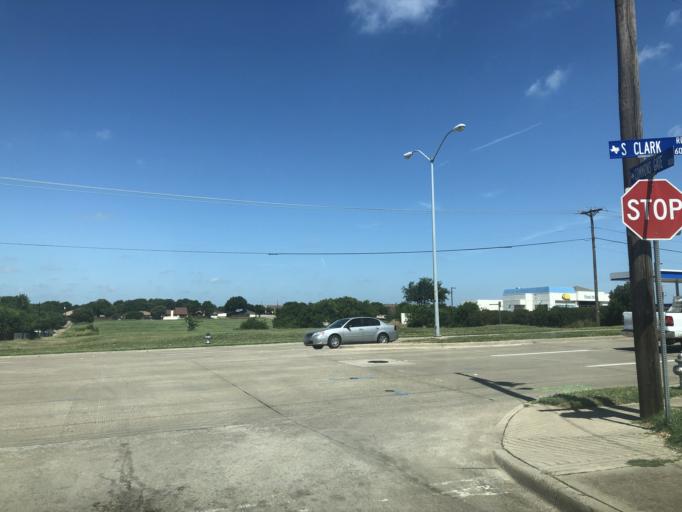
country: US
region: Texas
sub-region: Dallas County
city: Duncanville
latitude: 32.6461
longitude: -96.9426
